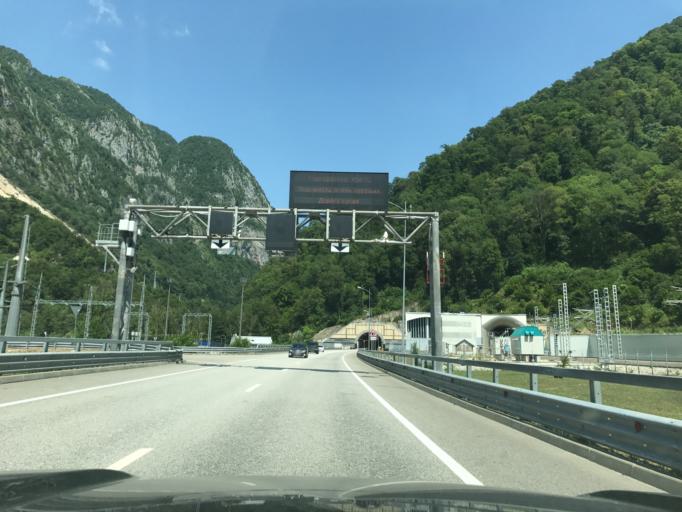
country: RU
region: Krasnodarskiy
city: Vysokoye
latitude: 43.5885
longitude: 40.0151
